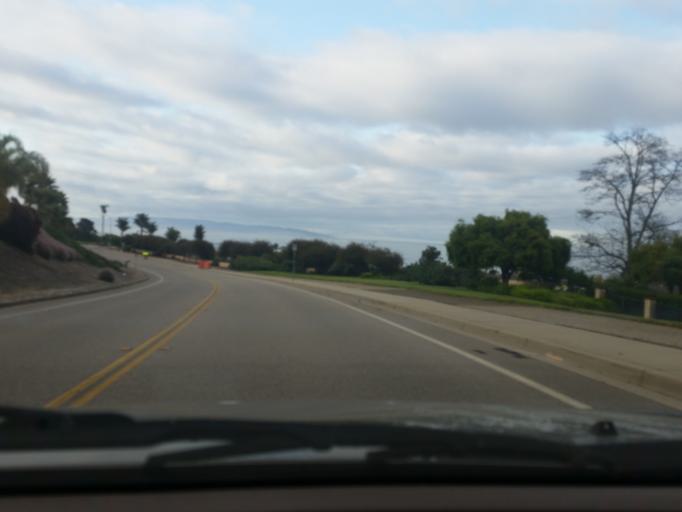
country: US
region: California
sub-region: San Luis Obispo County
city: Avila Beach
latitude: 35.1752
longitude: -120.6982
